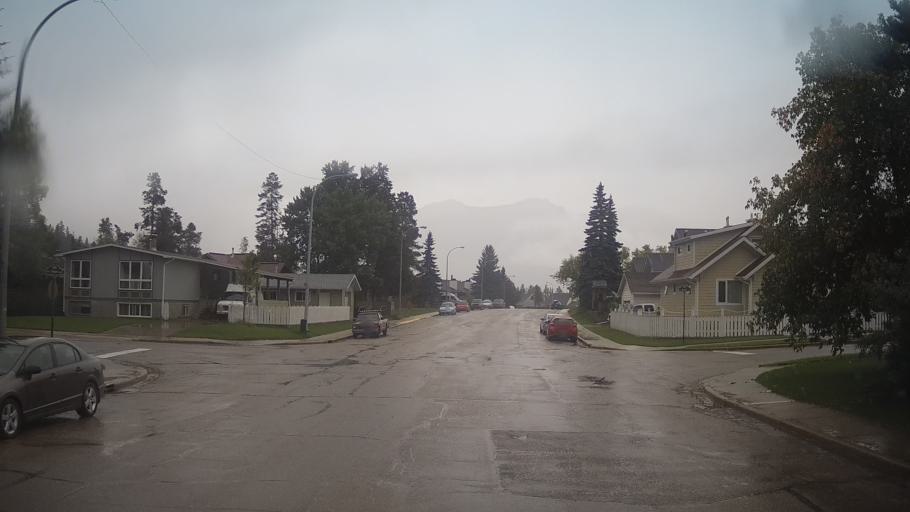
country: CA
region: Alberta
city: Jasper Park Lodge
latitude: 52.8830
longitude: -118.0831
